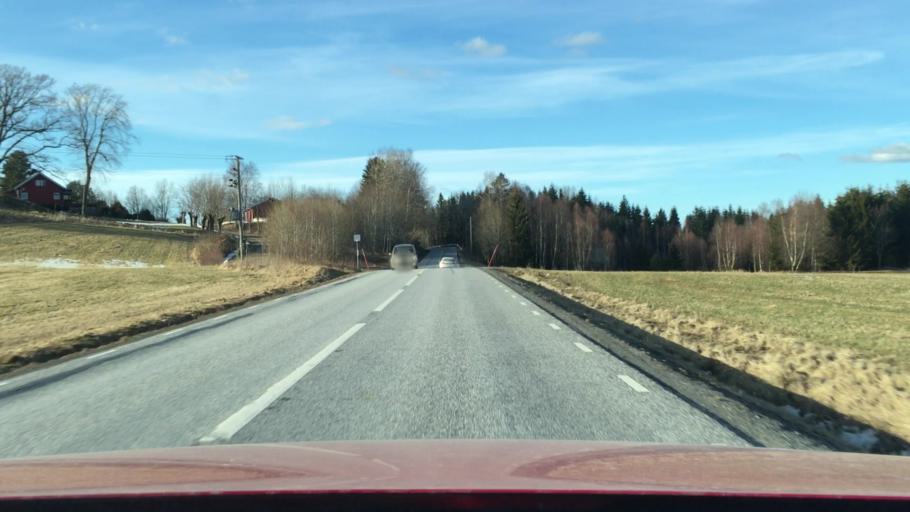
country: SE
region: Vaestra Goetaland
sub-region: Tanums Kommun
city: Tanumshede
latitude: 58.8074
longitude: 11.5526
